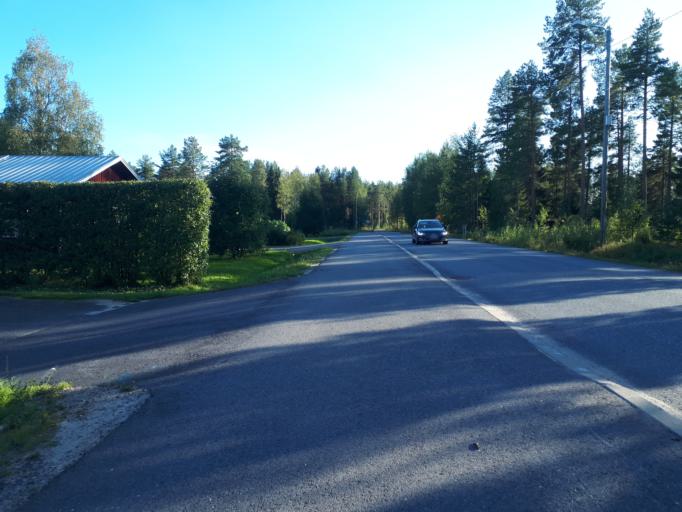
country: FI
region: Northern Ostrobothnia
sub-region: Oulunkaari
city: Ii
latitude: 65.3136
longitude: 25.3844
